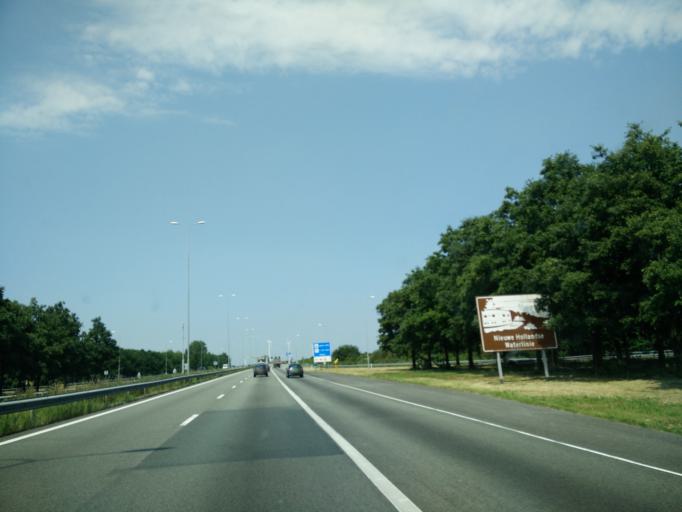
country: NL
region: Utrecht
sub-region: Gemeente Vianen
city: Vianen
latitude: 51.9923
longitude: 5.1115
